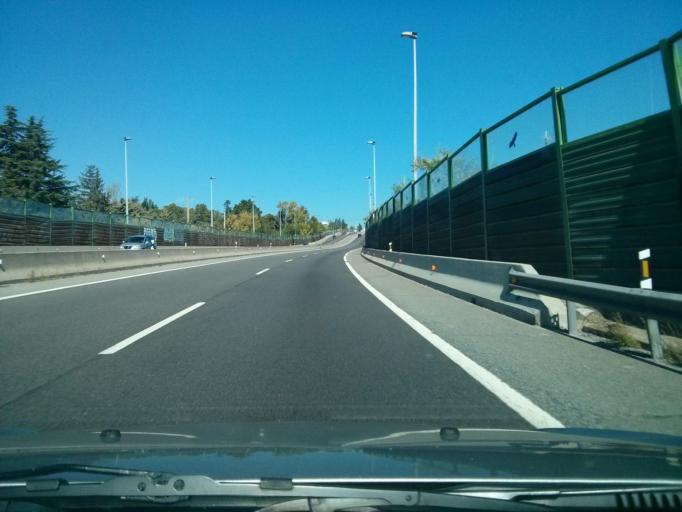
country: ES
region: Madrid
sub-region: Provincia de Madrid
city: Garganta de los Montes
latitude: 40.9280
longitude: -3.6227
